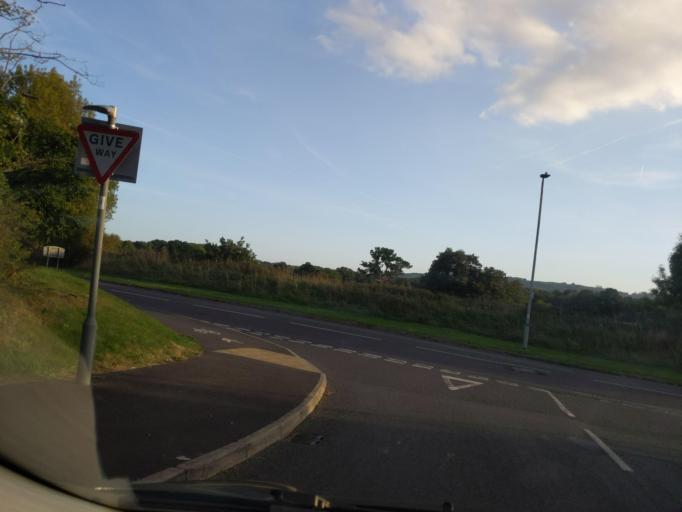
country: GB
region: England
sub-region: Devon
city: Bovey Tracey
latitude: 50.5905
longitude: -3.6613
